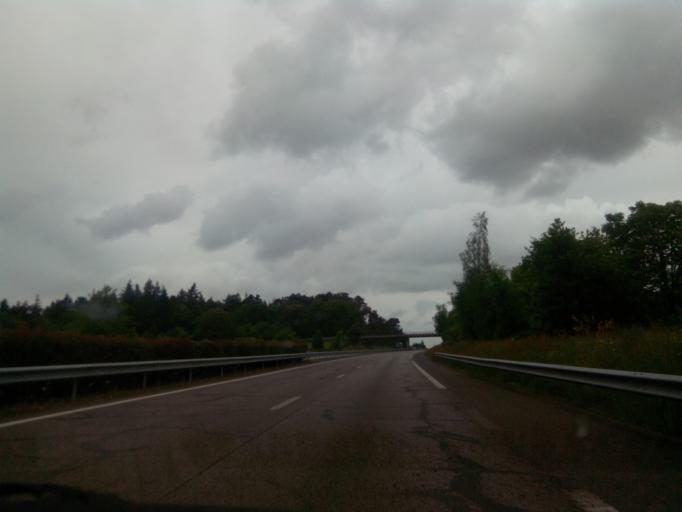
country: FR
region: Brittany
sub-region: Departement du Morbihan
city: Serent
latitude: 47.7937
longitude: -2.4522
